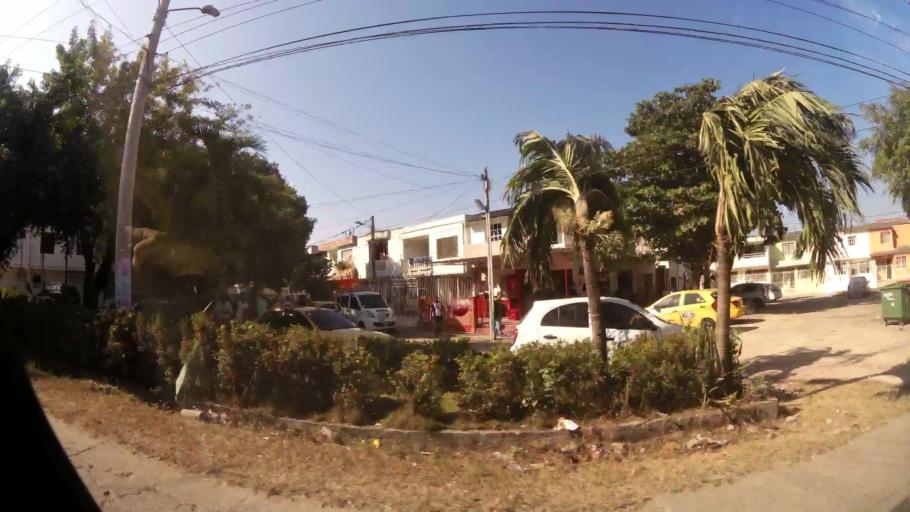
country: CO
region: Bolivar
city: Cartagena
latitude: 10.3949
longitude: -75.4923
